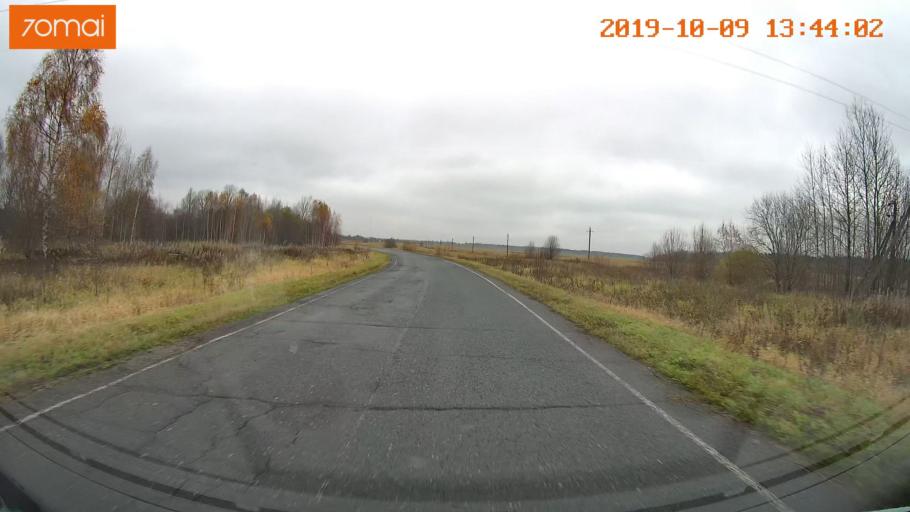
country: RU
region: Kostroma
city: Buy
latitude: 58.3630
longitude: 41.2064
